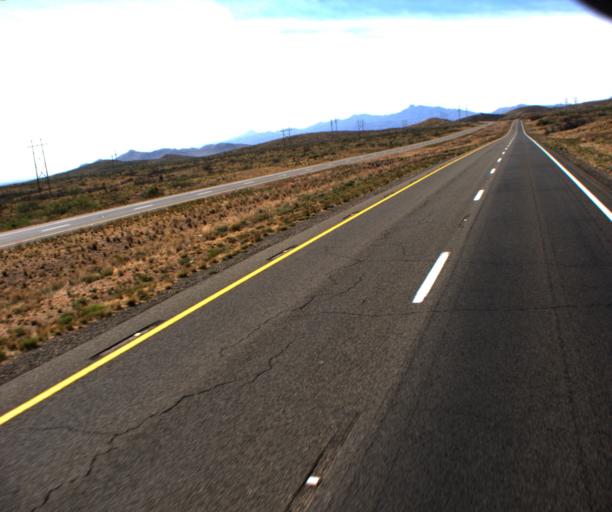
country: US
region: Arizona
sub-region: Graham County
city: Swift Trail Junction
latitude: 32.4846
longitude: -109.6734
